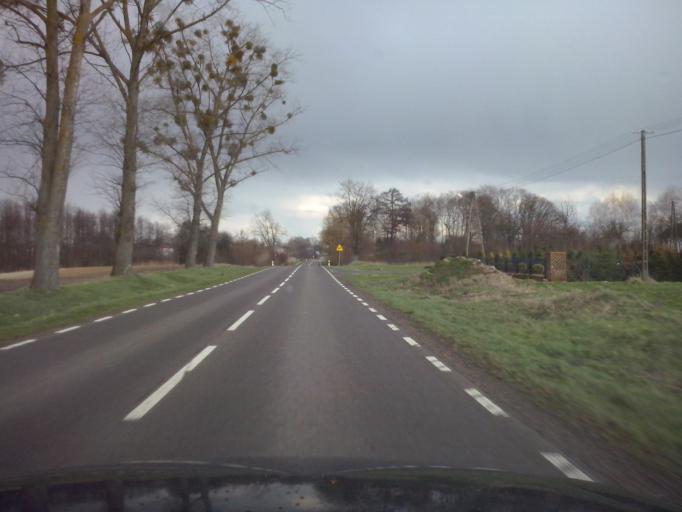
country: PL
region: Lublin Voivodeship
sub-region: Powiat krasnostawski
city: Krasnystaw
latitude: 51.0308
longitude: 23.2331
